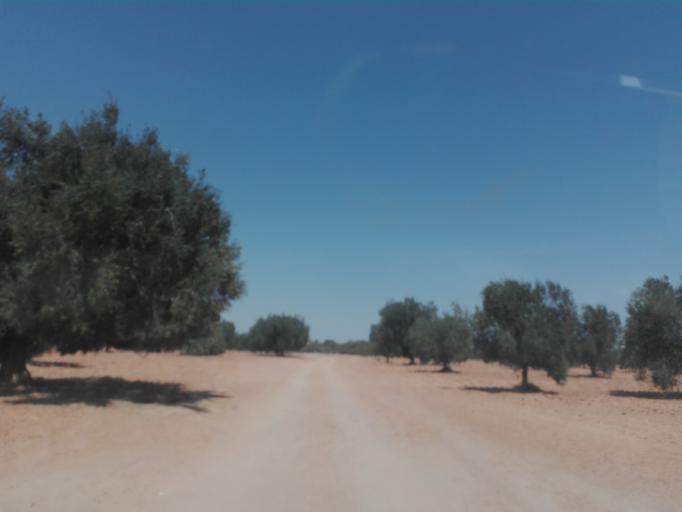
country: TN
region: Safaqis
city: Bi'r `Ali Bin Khalifah
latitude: 34.6468
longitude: 10.2622
